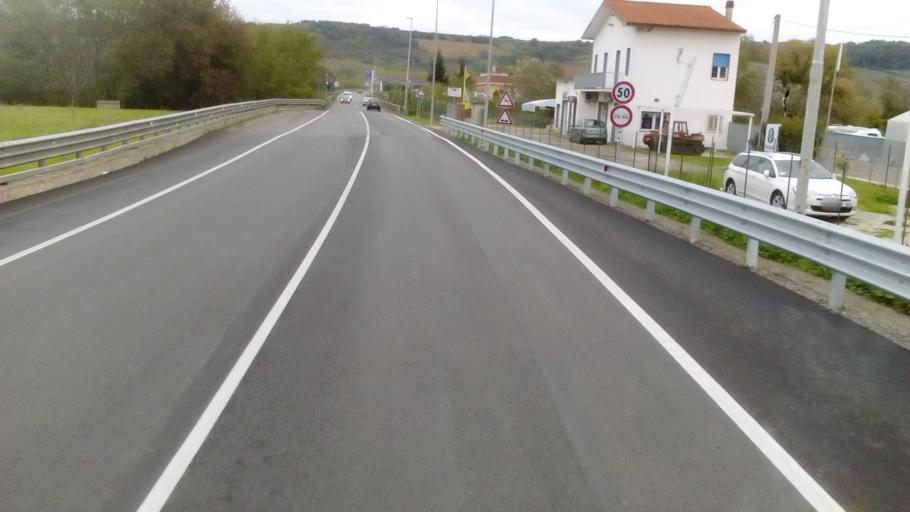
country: IT
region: Abruzzo
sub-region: Provincia di Chieti
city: Casalbordino-Miracoli
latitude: 42.1639
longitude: 14.6419
